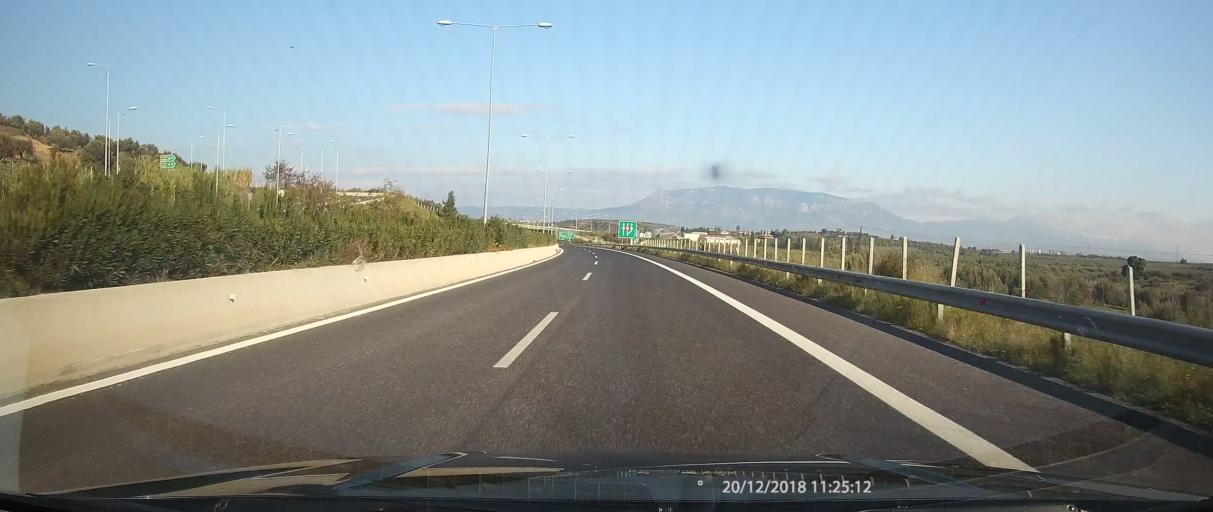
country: GR
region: Peloponnese
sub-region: Nomos Korinthias
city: Arkhaia Korinthos
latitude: 37.8923
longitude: 22.8965
